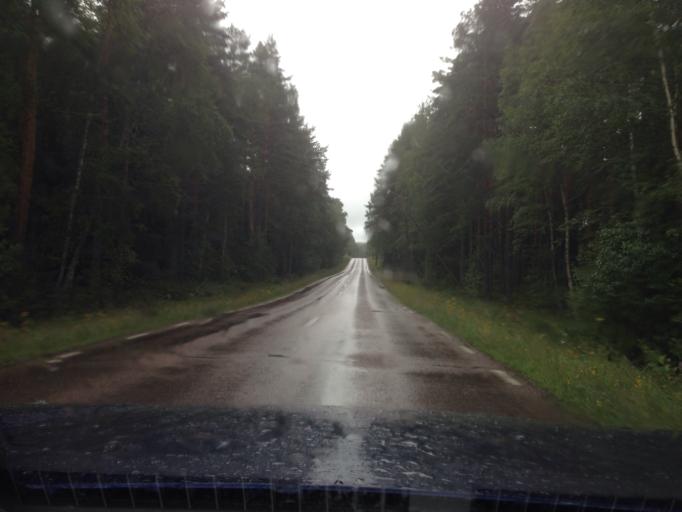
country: SE
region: Dalarna
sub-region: Ludvika Kommun
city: Grangesberg
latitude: 60.1572
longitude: 14.9735
